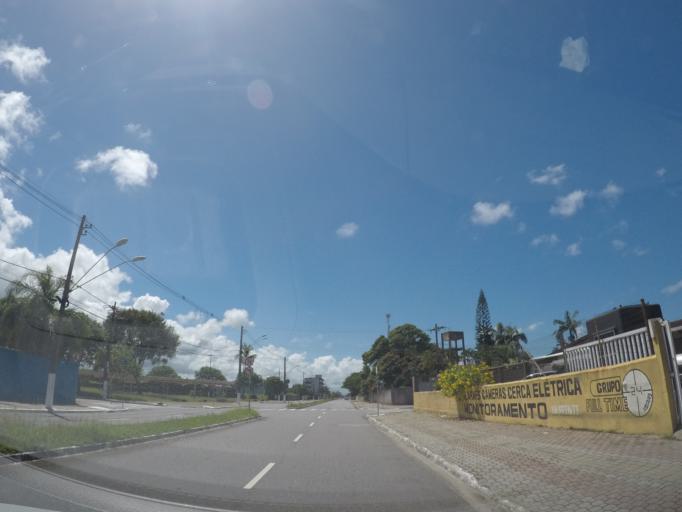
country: BR
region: Sao Paulo
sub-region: Mongagua
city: Mongagua
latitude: -24.0774
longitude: -46.5876
